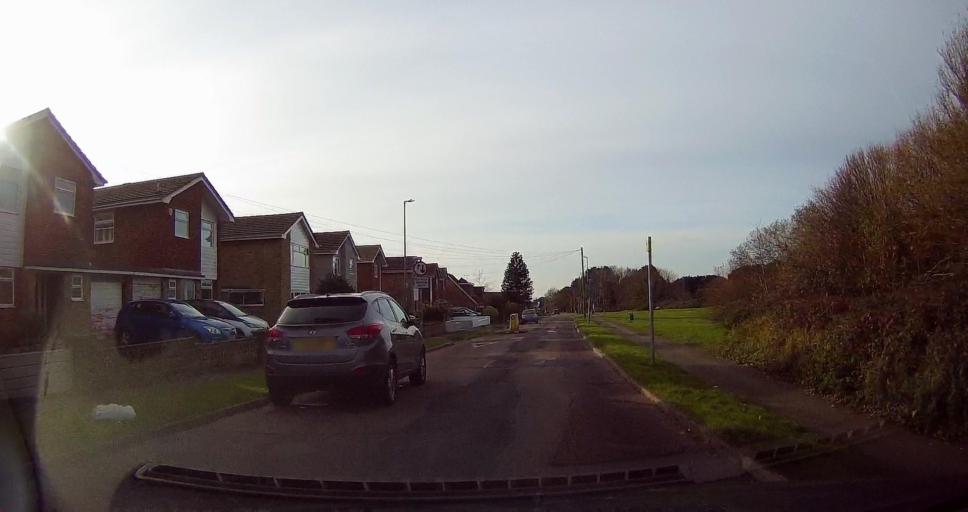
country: GB
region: England
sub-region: East Sussex
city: Peacehaven
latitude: 50.7995
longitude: -0.0064
